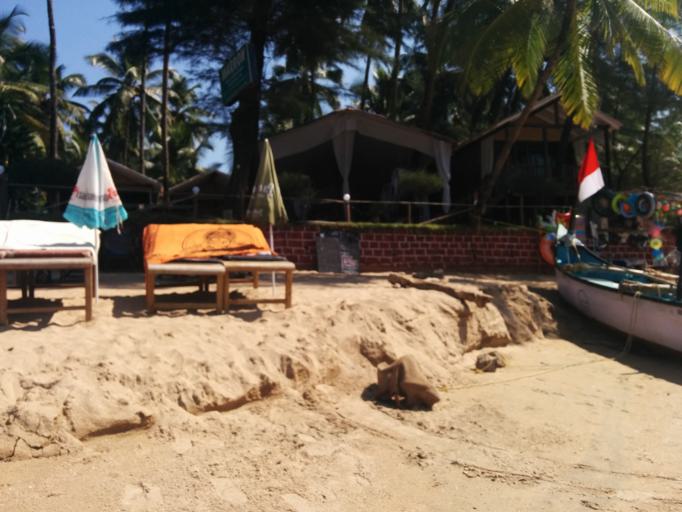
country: IN
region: Karnataka
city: Canacona
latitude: 15.0054
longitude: 74.0271
